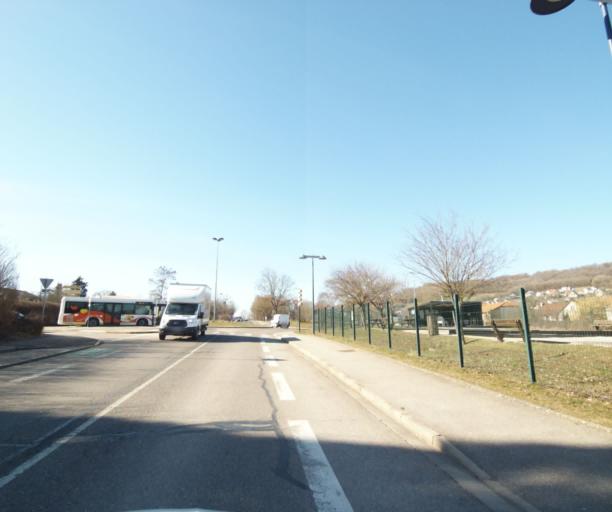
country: FR
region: Lorraine
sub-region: Departement de Meurthe-et-Moselle
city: Ludres
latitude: 48.6187
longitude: 6.1640
